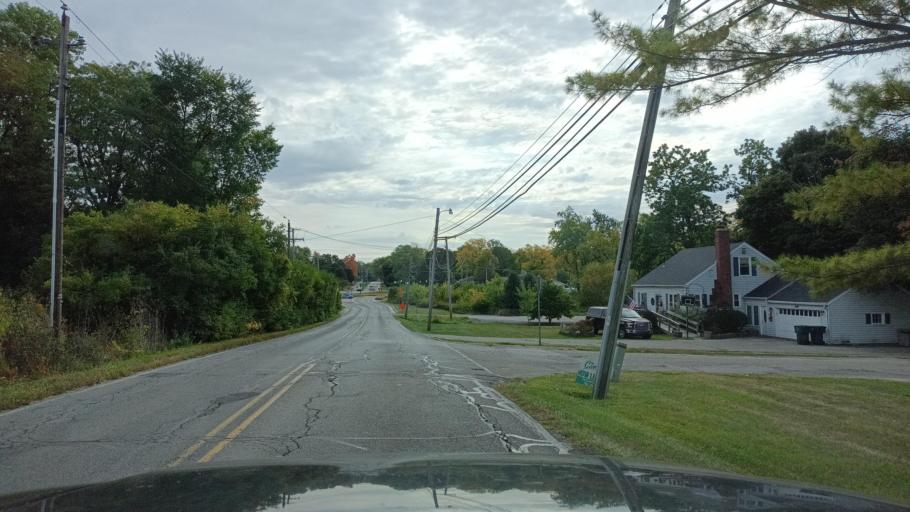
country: US
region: Indiana
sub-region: Delaware County
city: Yorktown
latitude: 40.2003
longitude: -85.4451
